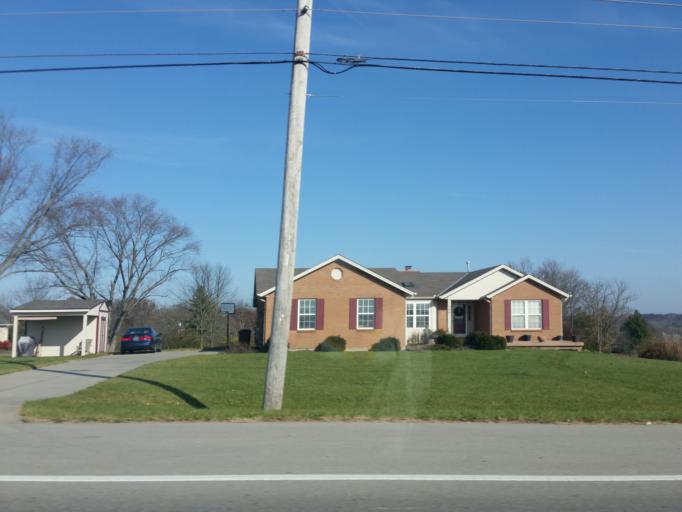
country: US
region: Ohio
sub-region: Butler County
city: Ross
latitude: 39.4047
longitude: -84.6666
